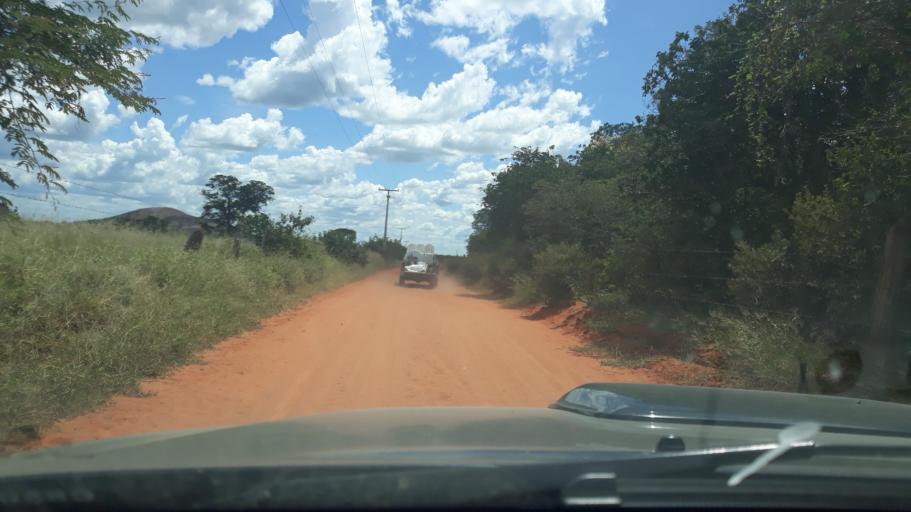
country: BR
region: Bahia
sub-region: Riacho De Santana
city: Riacho de Santana
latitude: -13.9056
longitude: -42.9123
